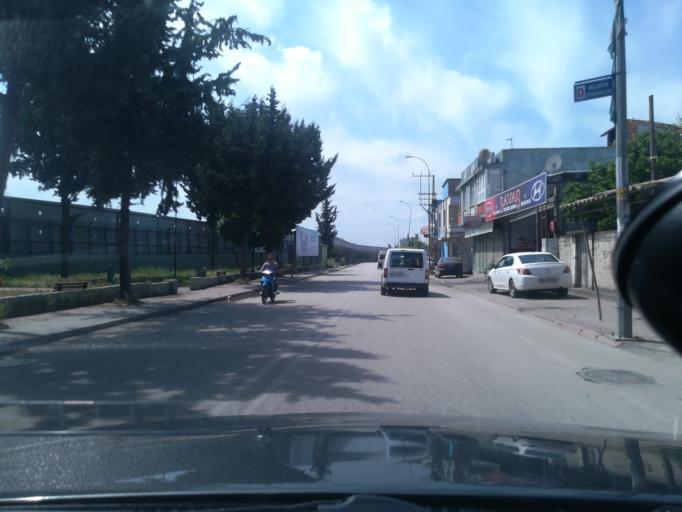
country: TR
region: Adana
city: Seyhan
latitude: 36.9925
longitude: 35.2876
